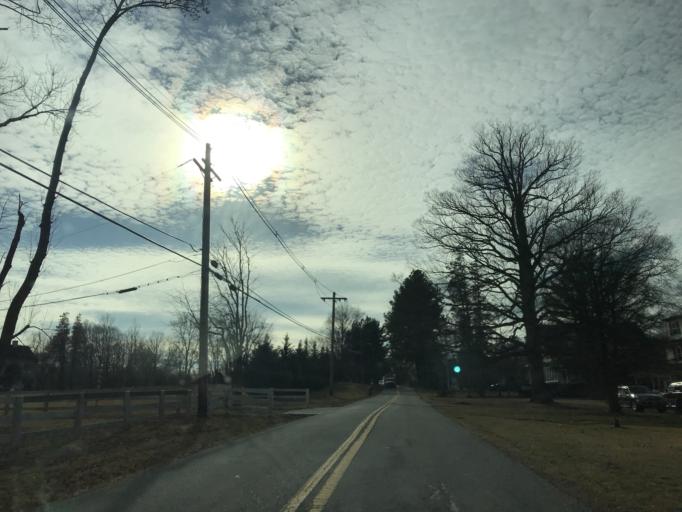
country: US
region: Maryland
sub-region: Baltimore County
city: Kingsville
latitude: 39.4421
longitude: -76.3959
